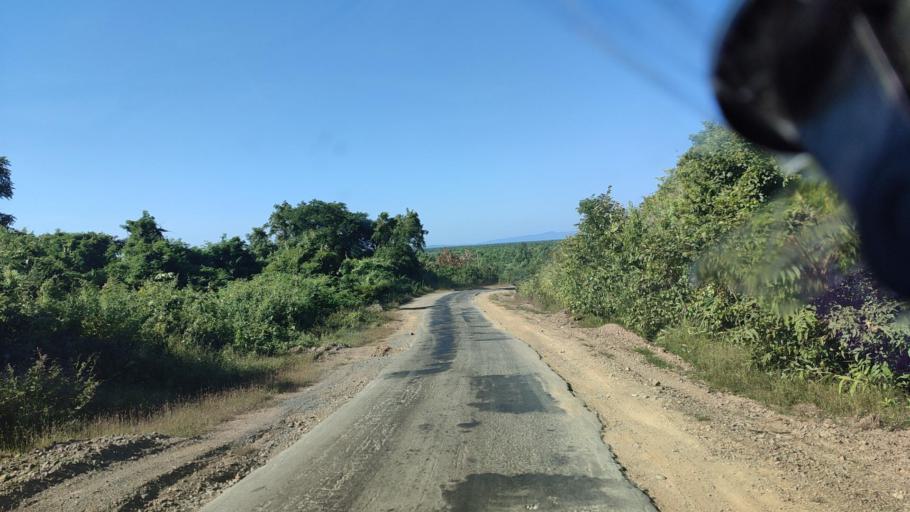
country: MM
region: Rakhine
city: Sittwe
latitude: 19.9328
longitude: 93.7616
